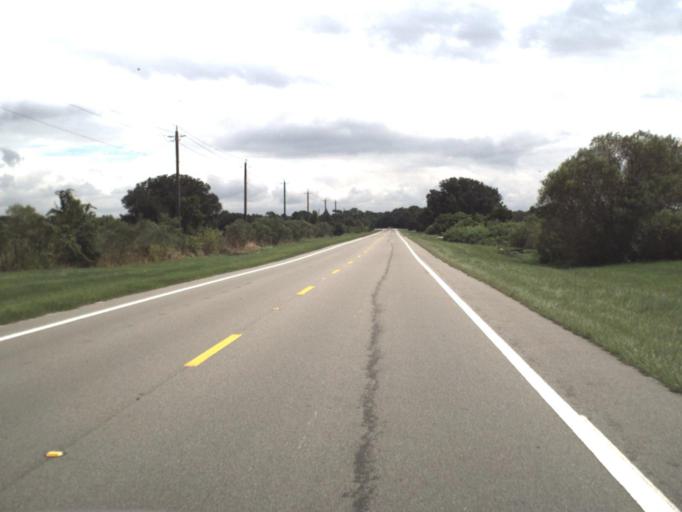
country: US
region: Florida
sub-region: Hillsborough County
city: Ruskin
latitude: 27.5869
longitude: -82.4049
